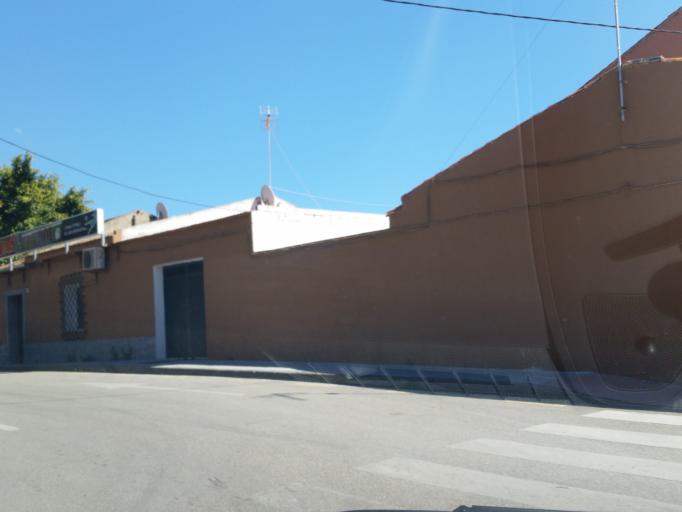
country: ES
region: Andalusia
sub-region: Provincia de Malaga
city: Torremolinos
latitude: 36.6672
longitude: -4.4750
